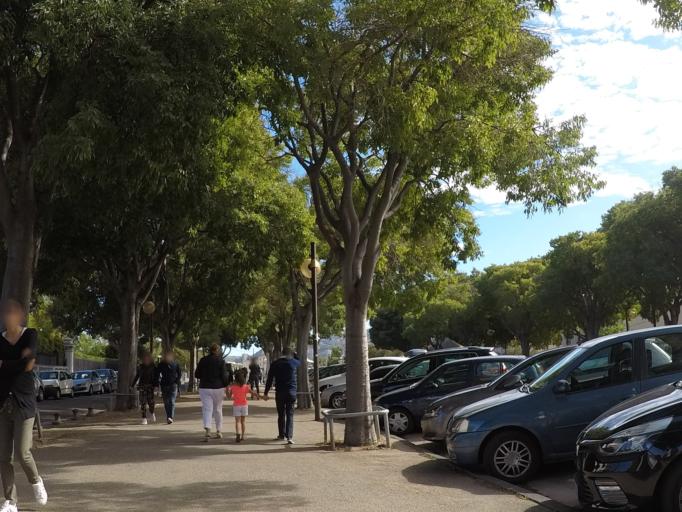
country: FR
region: Provence-Alpes-Cote d'Azur
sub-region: Departement des Bouches-du-Rhone
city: Marseille 08
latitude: 43.2625
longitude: 5.3788
